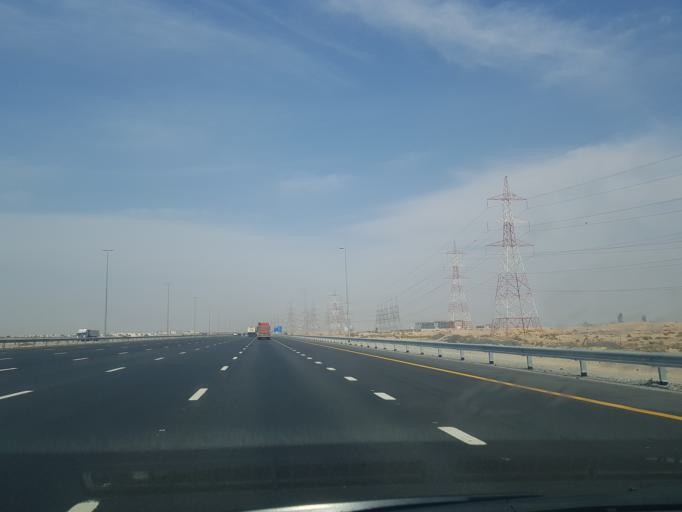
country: AE
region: Ash Shariqah
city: Sharjah
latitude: 25.2784
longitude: 55.5851
